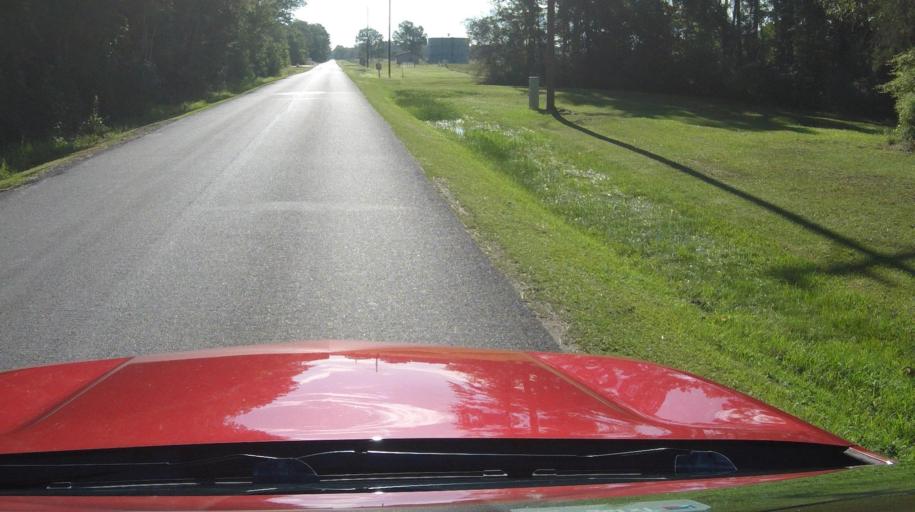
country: US
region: Louisiana
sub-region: Allen Parish
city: Oberlin
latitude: 30.5673
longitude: -92.7959
